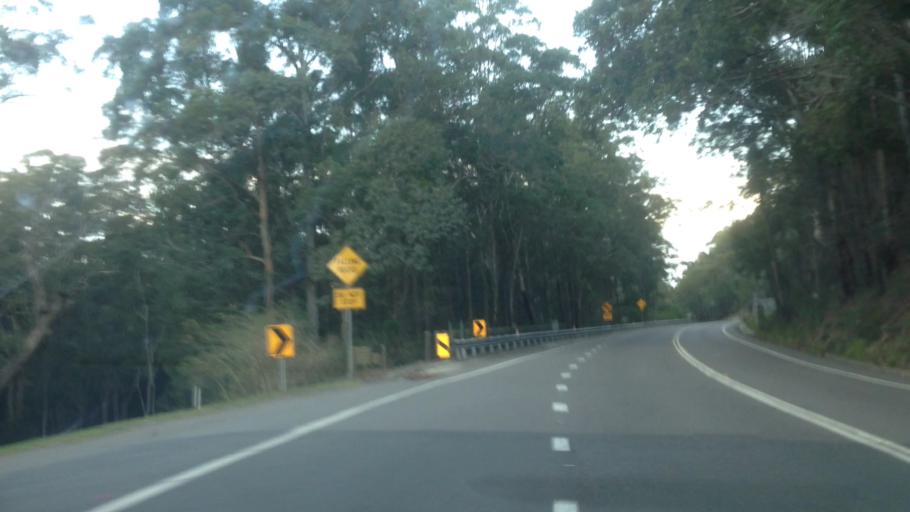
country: AU
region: New South Wales
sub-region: Lake Macquarie Shire
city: Cooranbong
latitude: -32.9649
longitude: 151.4794
